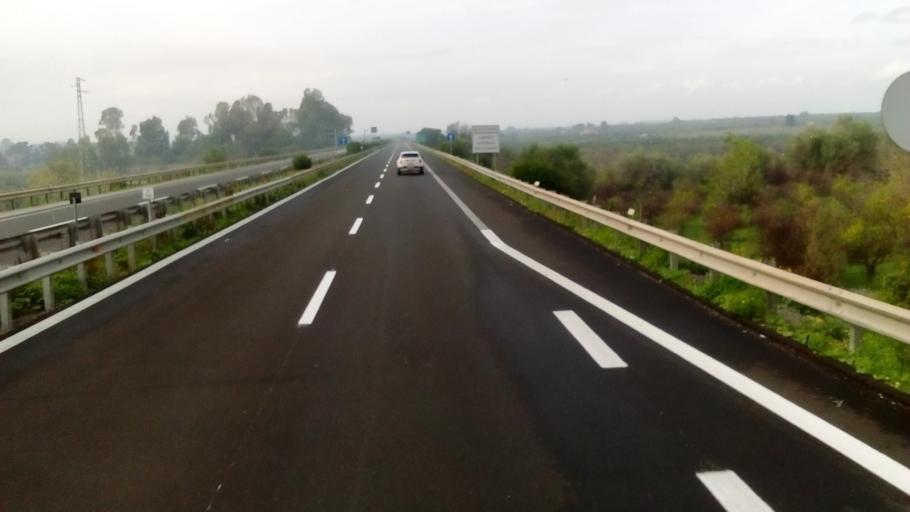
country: IT
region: Sicily
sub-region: Catania
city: Motta Sant'Anastasia
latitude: 37.4647
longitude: 14.9338
